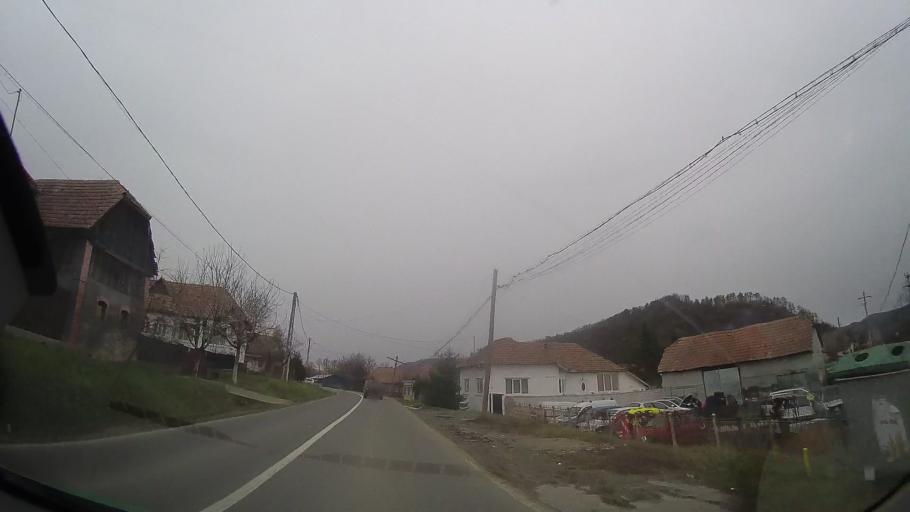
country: RO
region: Mures
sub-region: Comuna Ceausu de Campie
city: Ceausu de Campie
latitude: 46.6172
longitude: 24.5258
